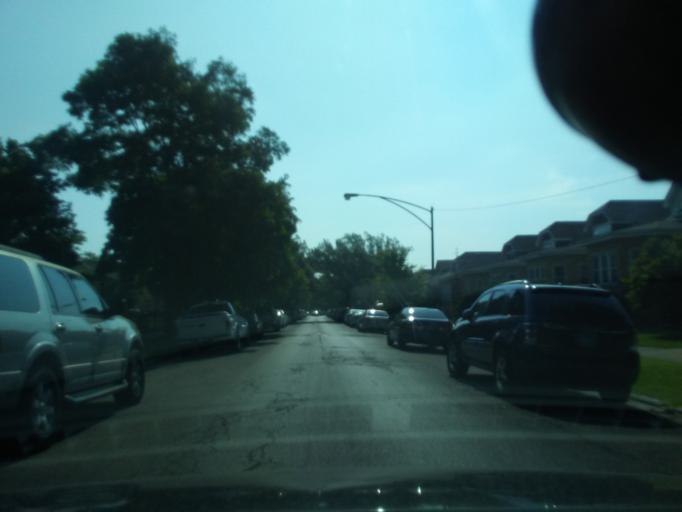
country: US
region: Illinois
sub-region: Cook County
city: Oak Park
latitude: 41.9278
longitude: -87.7585
